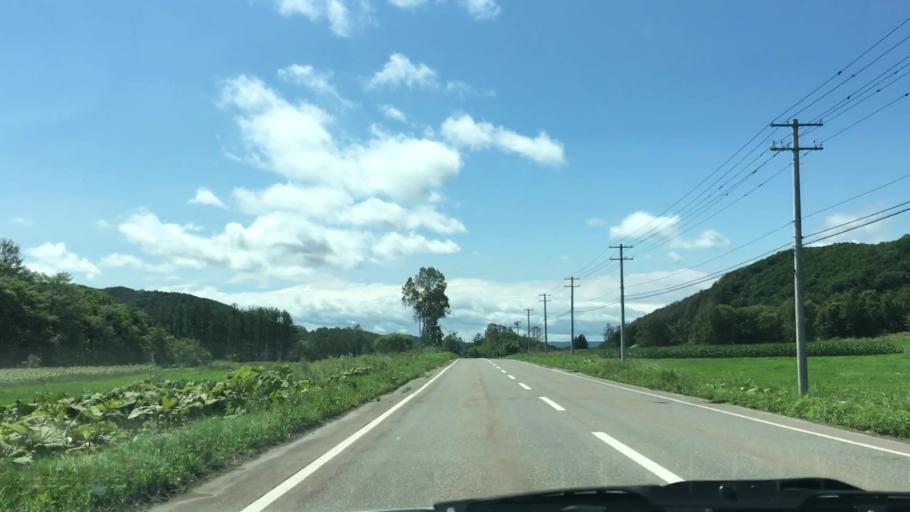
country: JP
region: Hokkaido
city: Kitami
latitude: 43.2963
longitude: 143.6742
